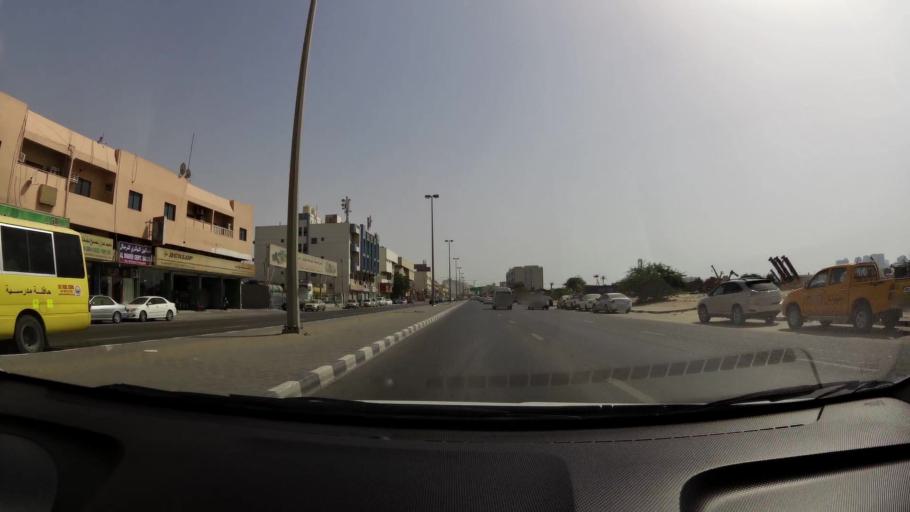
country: AE
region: Ash Shariqah
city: Sharjah
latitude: 25.3002
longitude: 55.4125
